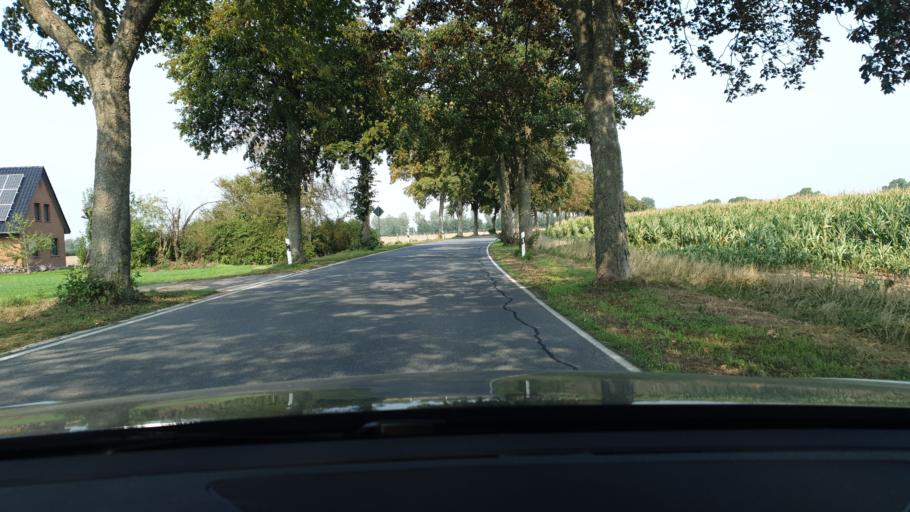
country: DE
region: North Rhine-Westphalia
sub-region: Regierungsbezirk Dusseldorf
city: Kranenburg
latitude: 51.8289
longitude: 6.0308
